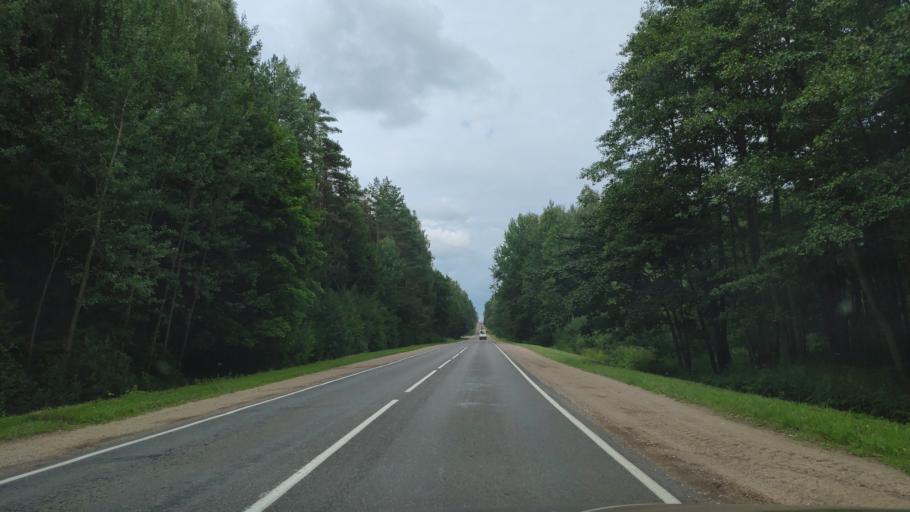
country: BY
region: Minsk
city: Novosel'ye
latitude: 53.9326
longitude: 27.2435
